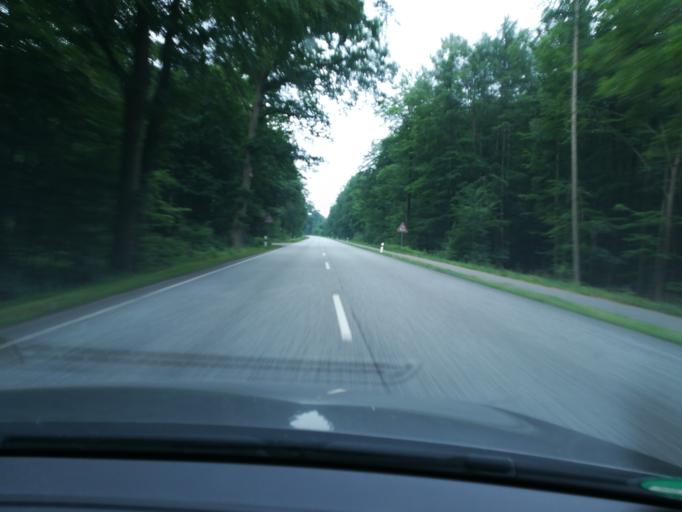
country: DE
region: Schleswig-Holstein
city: Brunstorf
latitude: 53.5318
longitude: 10.4335
